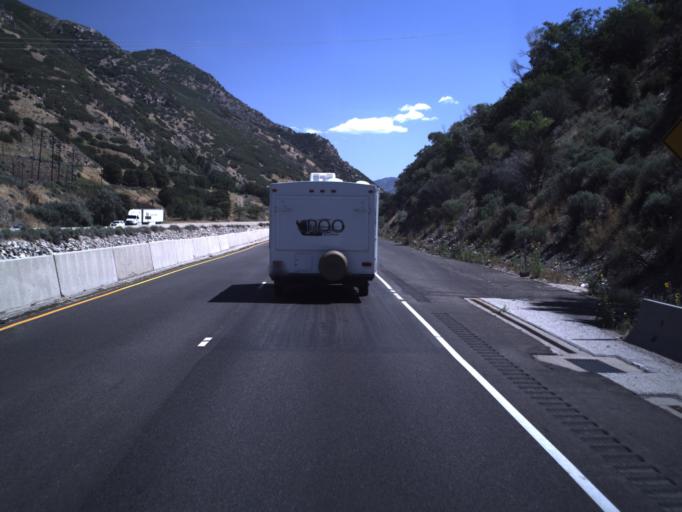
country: US
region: Utah
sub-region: Weber County
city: Uintah
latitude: 41.1371
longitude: -111.8827
